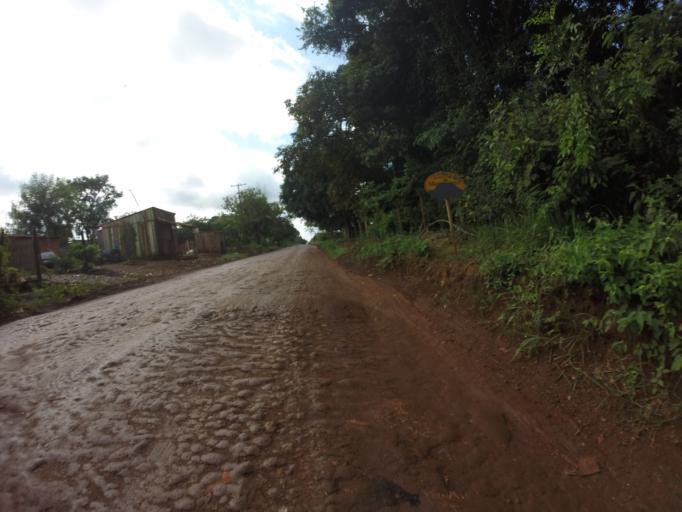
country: PY
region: Alto Parana
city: Ciudad del Este
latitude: -25.4100
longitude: -54.6629
